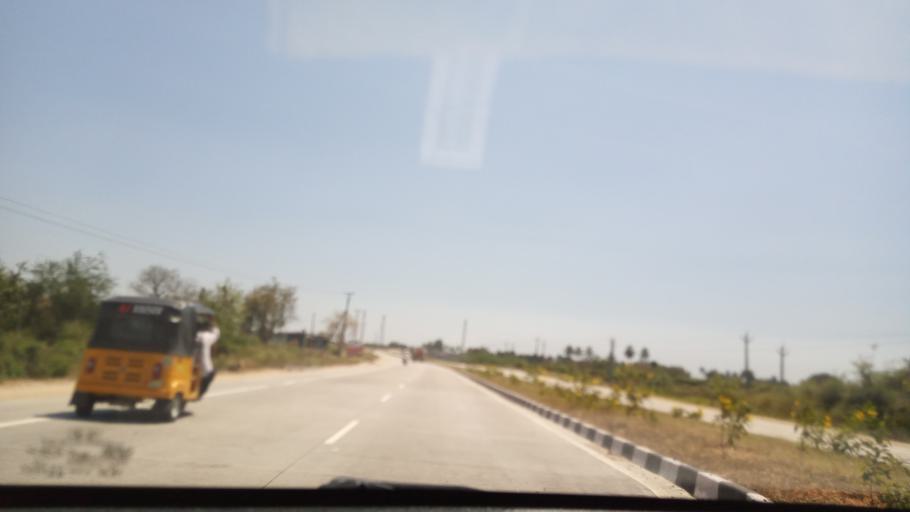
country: IN
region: Andhra Pradesh
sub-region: Chittoor
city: Chittoor
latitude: 13.2024
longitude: 78.9501
